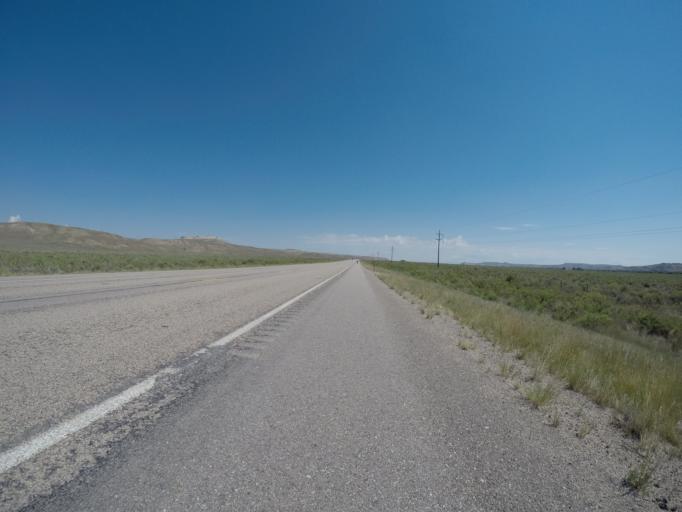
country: US
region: Wyoming
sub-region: Sublette County
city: Marbleton
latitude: 42.3579
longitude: -110.1560
